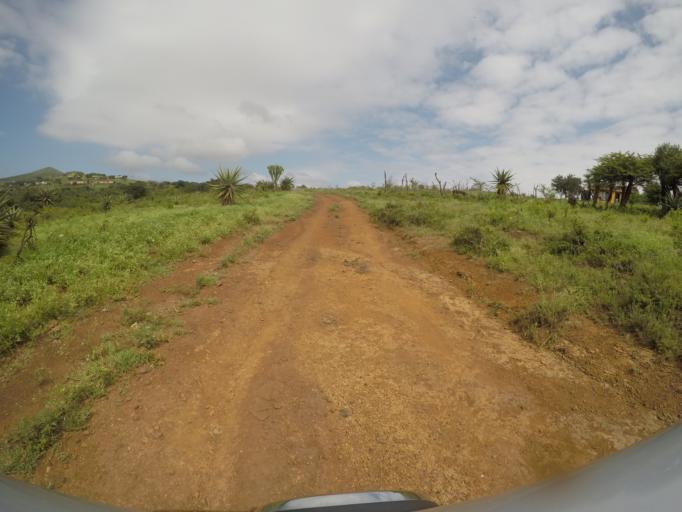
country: ZA
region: KwaZulu-Natal
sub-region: uThungulu District Municipality
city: Empangeni
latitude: -28.6211
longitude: 31.8734
